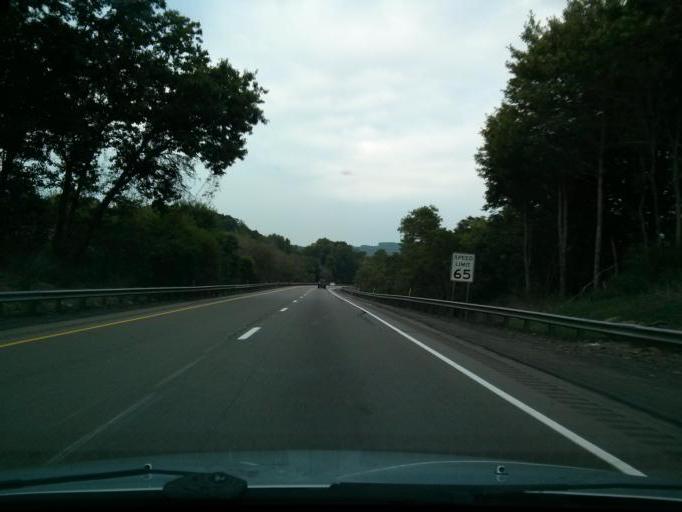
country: US
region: Pennsylvania
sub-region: Jefferson County
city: Brookville
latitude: 41.1681
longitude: -79.0379
